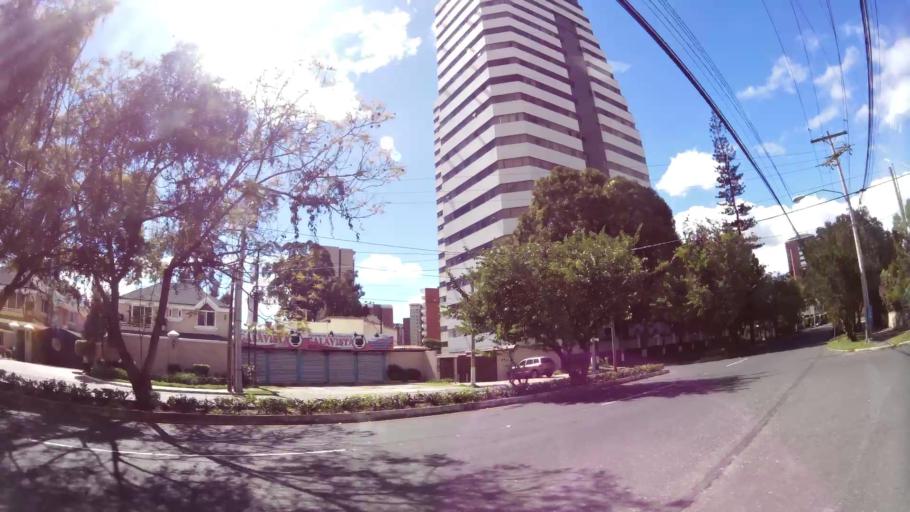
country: GT
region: Guatemala
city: Santa Catarina Pinula
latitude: 14.5791
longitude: -90.5183
